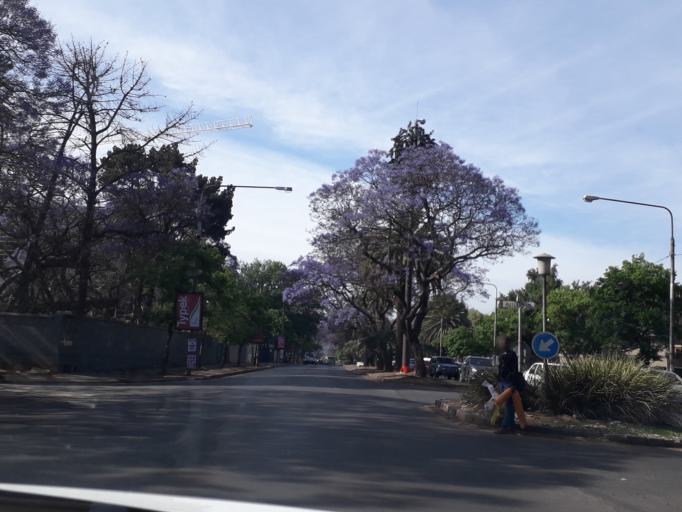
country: ZA
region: Gauteng
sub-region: City of Johannesburg Metropolitan Municipality
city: Johannesburg
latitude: -26.1514
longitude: 28.0453
